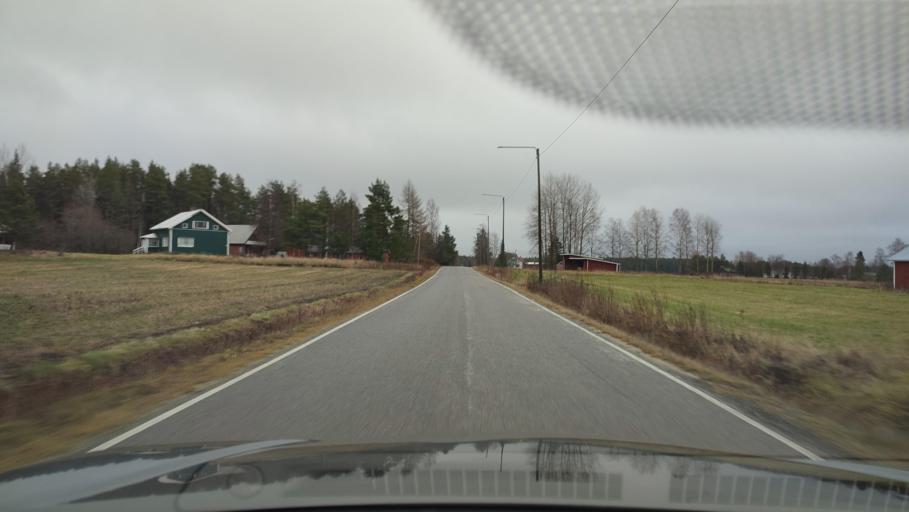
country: FI
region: Southern Ostrobothnia
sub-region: Suupohja
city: Isojoki
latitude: 62.1812
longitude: 21.9196
